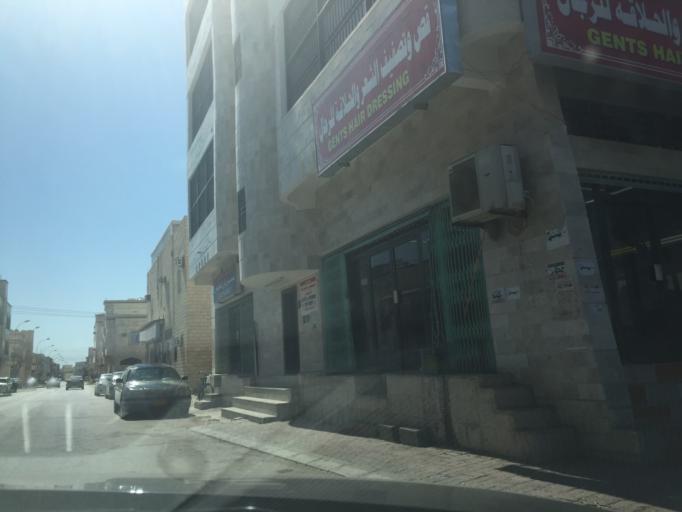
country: OM
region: Zufar
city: Salalah
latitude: 17.0257
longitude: 54.1565
